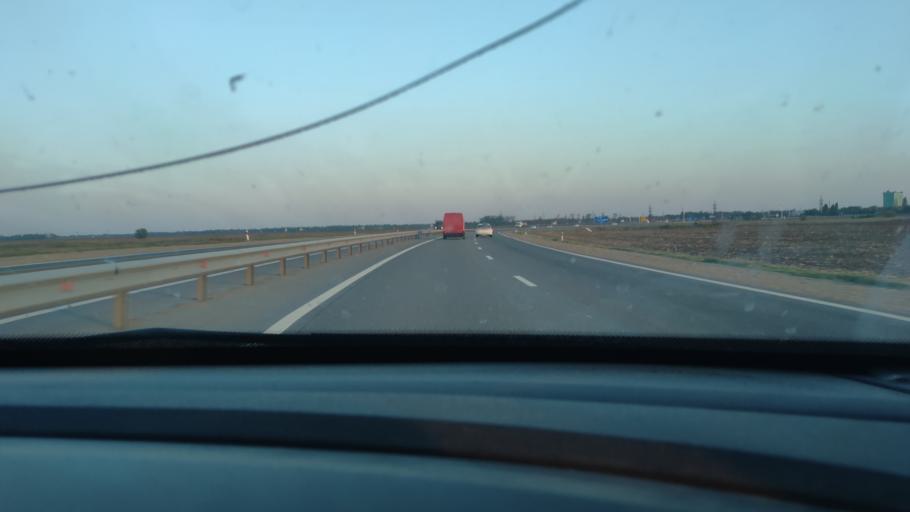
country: RU
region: Krasnodarskiy
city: Timashevsk
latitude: 45.6339
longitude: 38.9794
